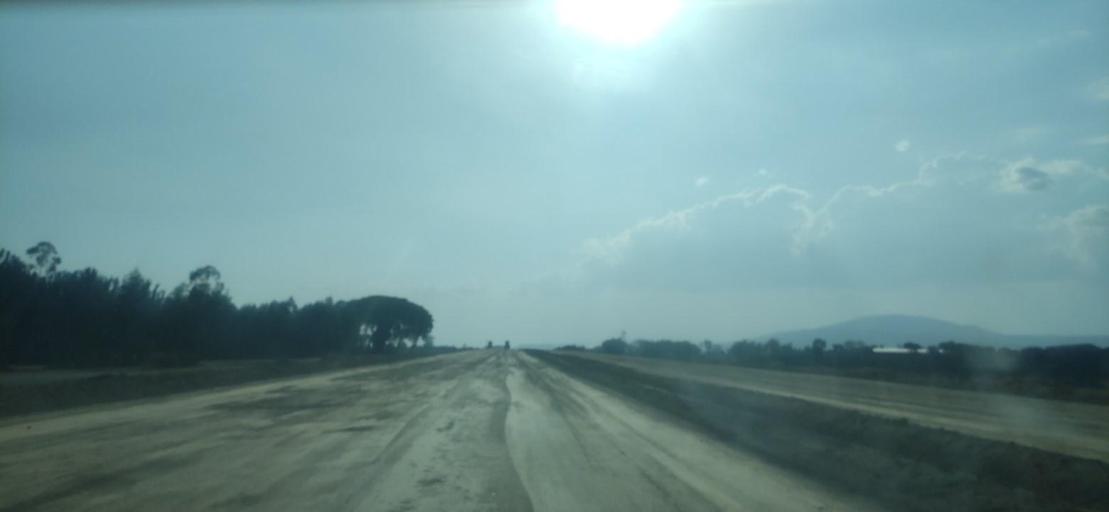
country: ET
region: Oromiya
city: Shashemene
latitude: 7.2030
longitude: 38.5397
